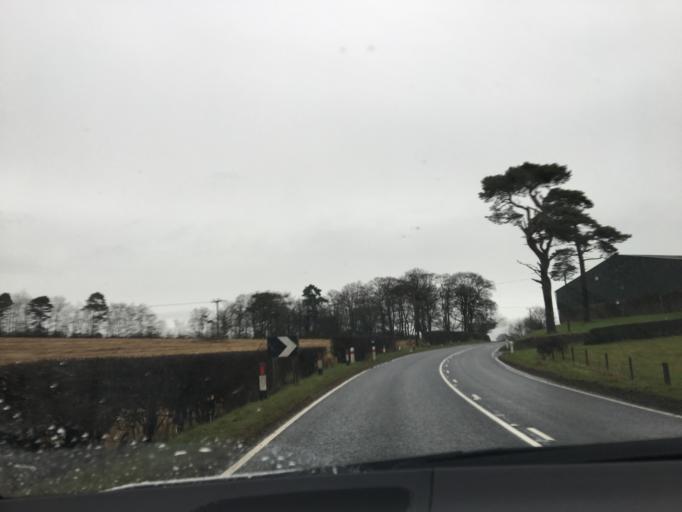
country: GB
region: Scotland
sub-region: Stirling
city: Doune
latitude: 56.1721
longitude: -4.0663
